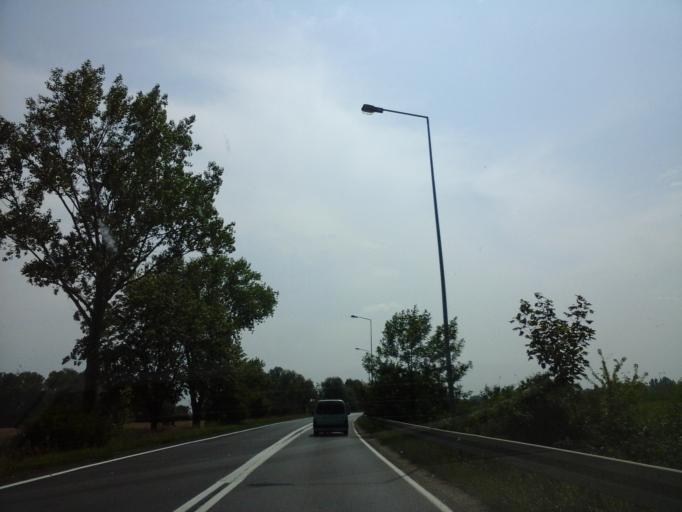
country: PL
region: Lower Silesian Voivodeship
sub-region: Powiat wroclawski
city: Zorawina
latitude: 50.9727
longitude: 17.0716
